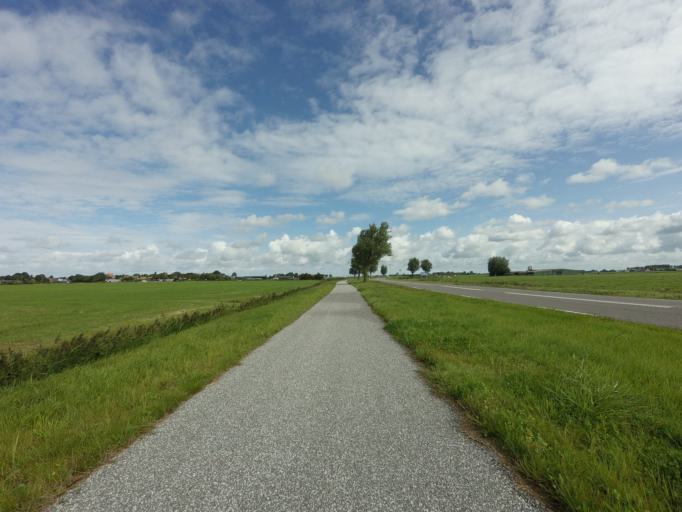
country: NL
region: Friesland
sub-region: Sudwest Fryslan
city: Makkum
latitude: 53.0781
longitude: 5.4259
